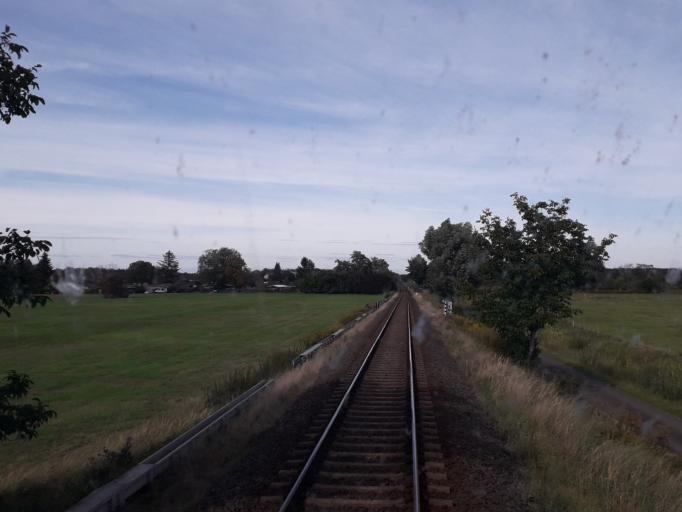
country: DE
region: Brandenburg
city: Kremmen
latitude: 52.7590
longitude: 13.0373
